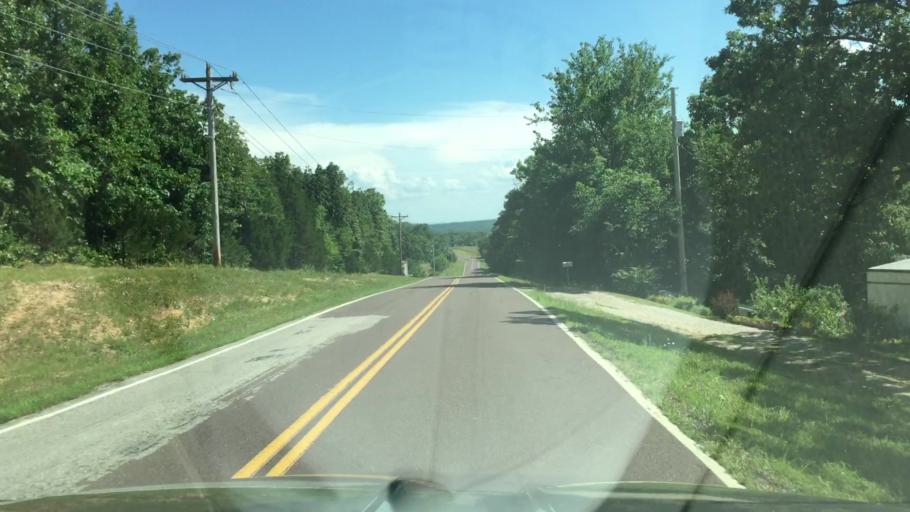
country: US
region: Missouri
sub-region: Miller County
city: Tuscumbia
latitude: 38.1135
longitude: -92.4722
